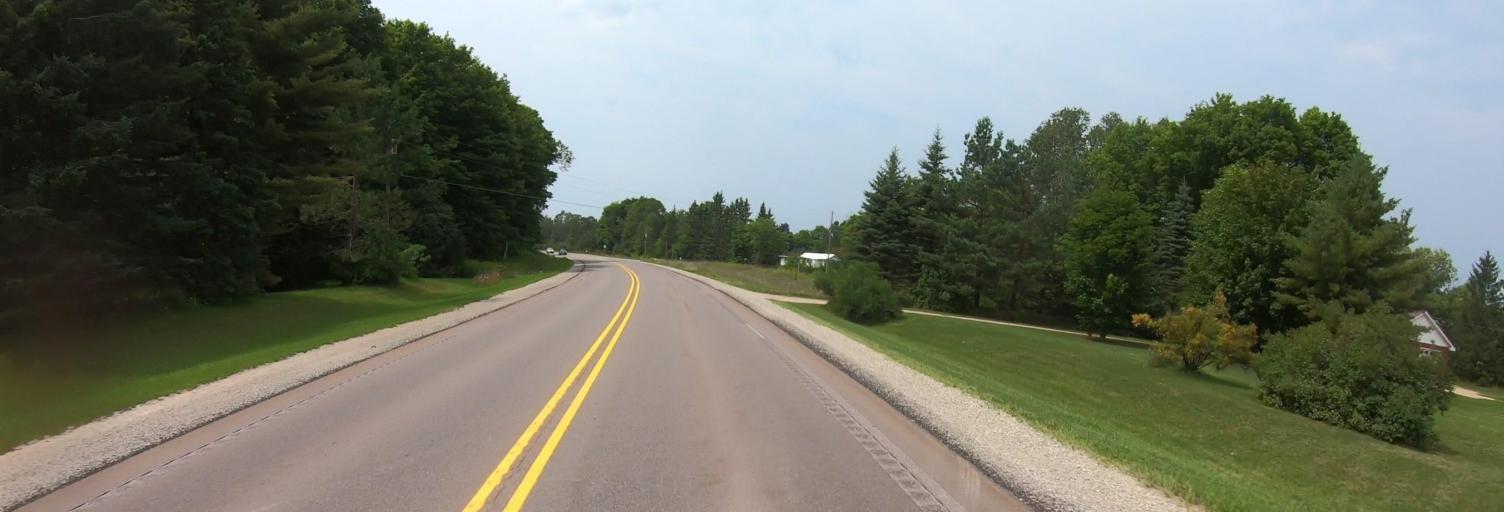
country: US
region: Michigan
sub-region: Alger County
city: Munising
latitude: 46.3537
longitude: -86.9563
